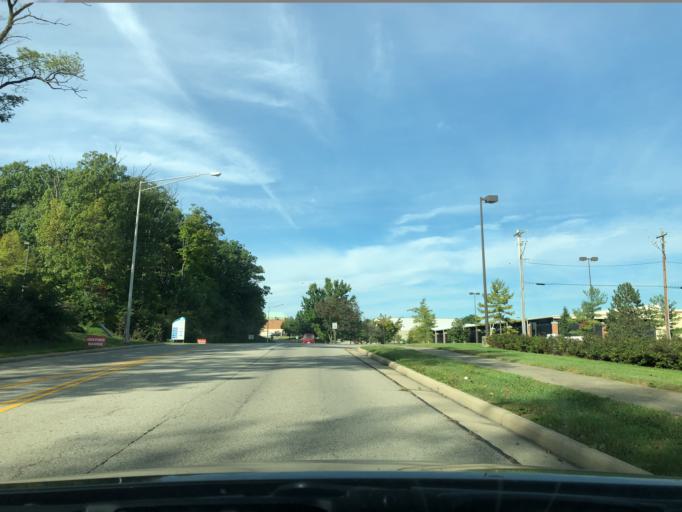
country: US
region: Ohio
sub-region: Hamilton County
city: Glendale
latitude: 39.2838
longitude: -84.4627
